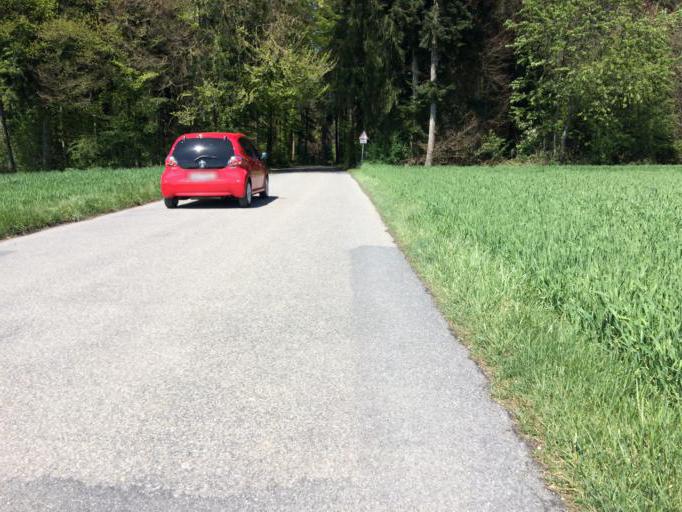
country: CH
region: Bern
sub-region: Bern-Mittelland District
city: Rubigen
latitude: 46.9230
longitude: 7.5386
